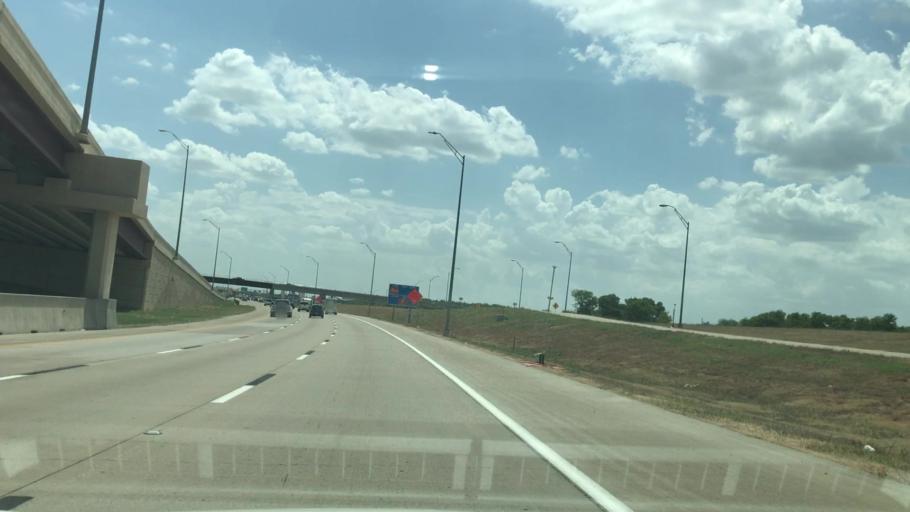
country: US
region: Texas
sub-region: Tarrant County
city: Grapevine
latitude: 32.9319
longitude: -97.0457
